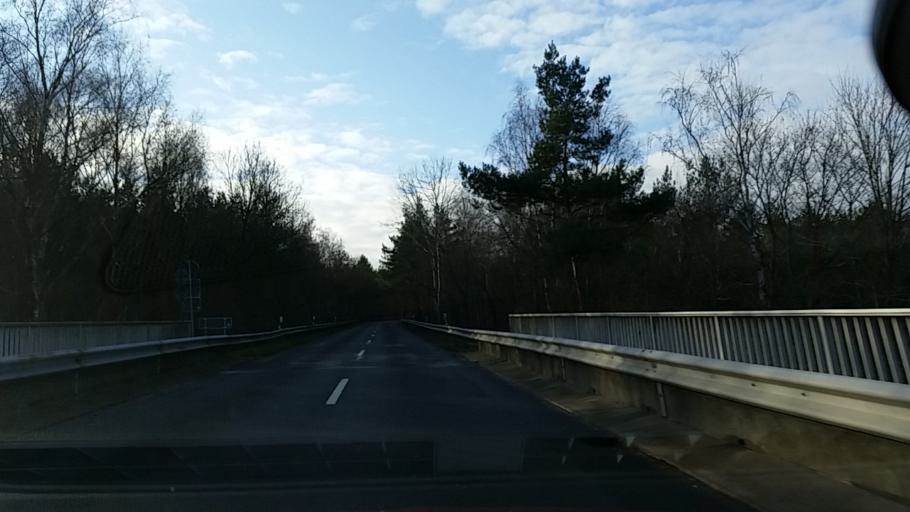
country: DE
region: Lower Saxony
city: Wieren
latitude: 52.8846
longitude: 10.6302
